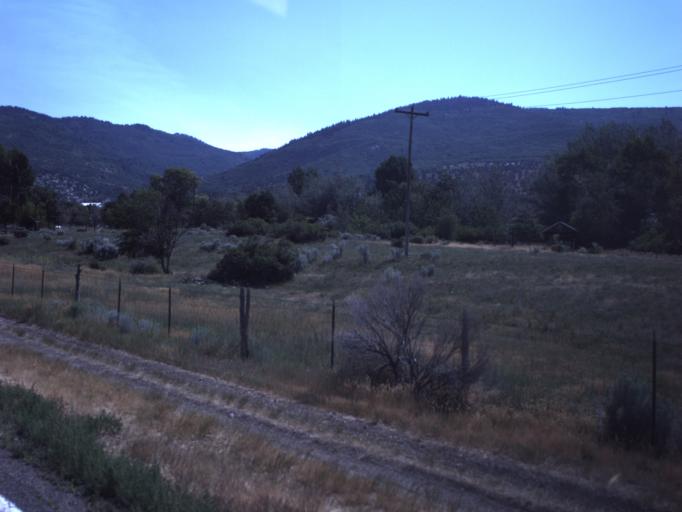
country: US
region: Utah
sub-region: Sanpete County
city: Fairview
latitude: 39.6363
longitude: -111.4259
